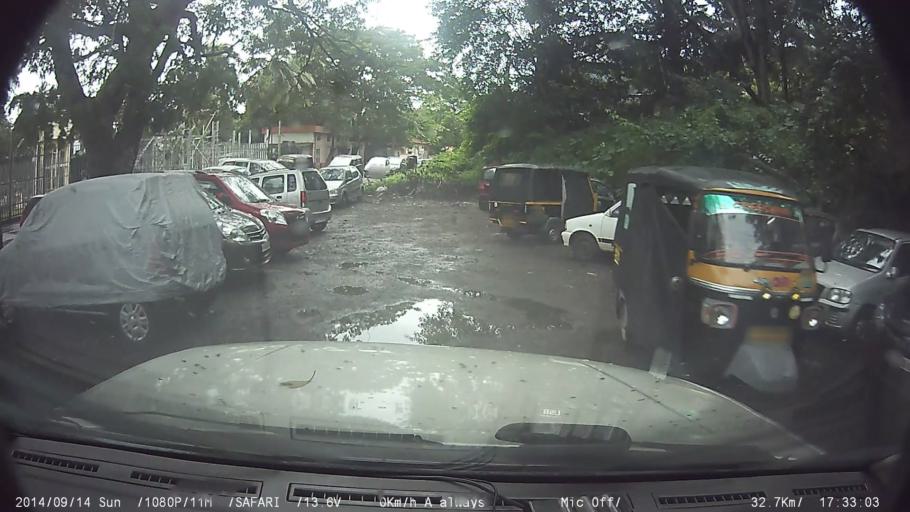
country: IN
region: Kerala
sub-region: Kottayam
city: Kottayam
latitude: 9.5939
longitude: 76.5328
